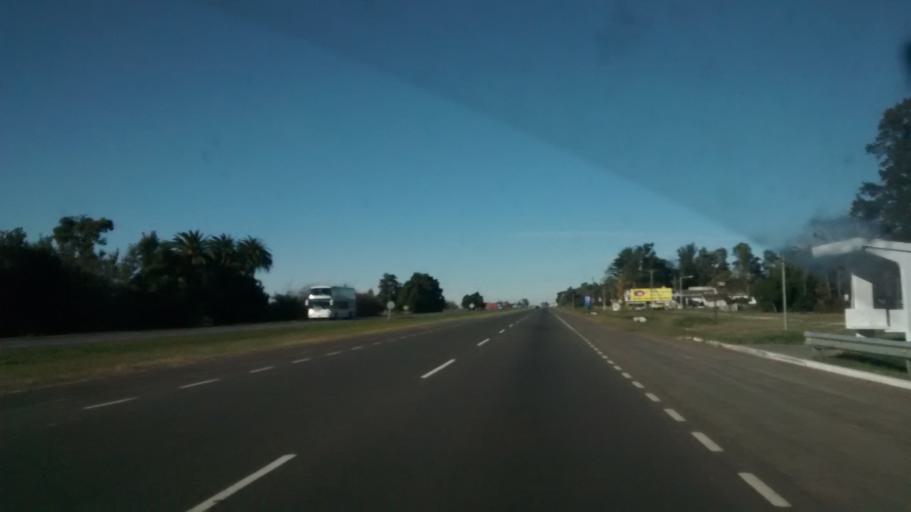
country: AR
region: Buenos Aires
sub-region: Partido de Chascomus
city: Chascomus
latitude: -35.7719
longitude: -57.9294
